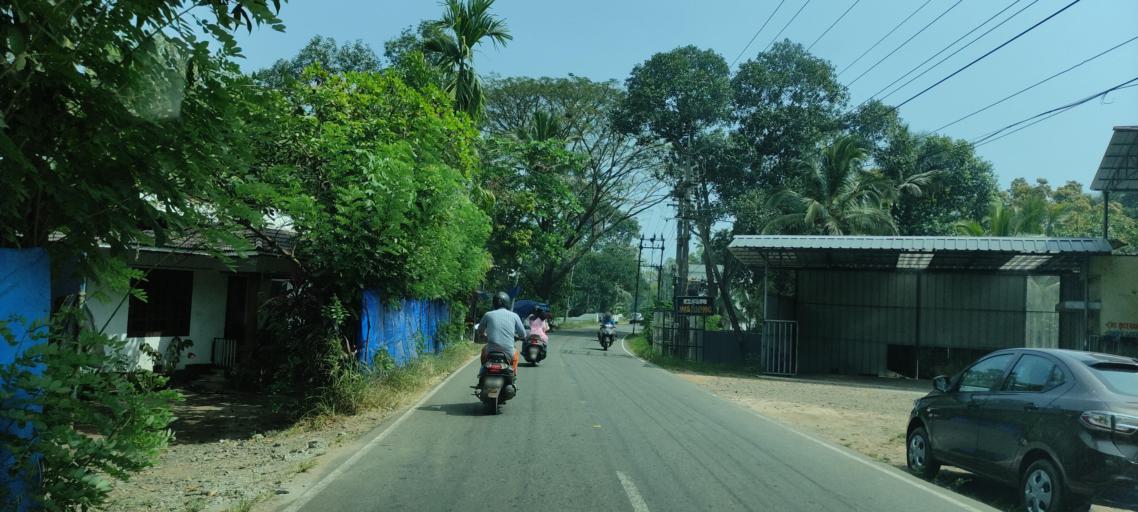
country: IN
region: Kerala
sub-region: Alappuzha
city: Shertallai
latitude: 9.6556
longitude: 76.3526
